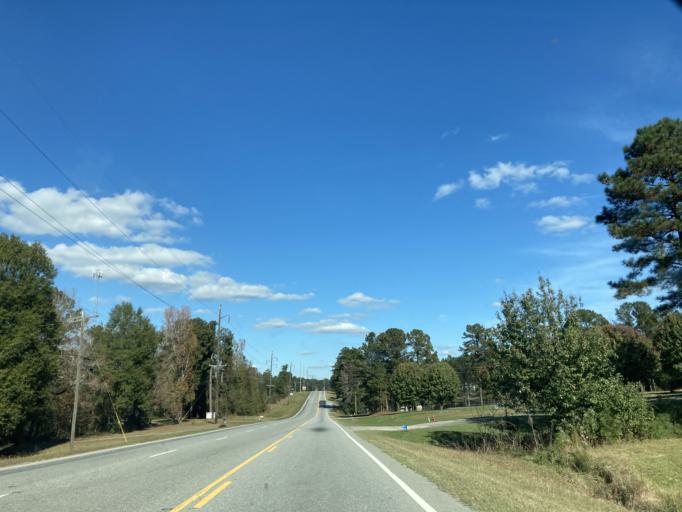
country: US
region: Georgia
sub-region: Jones County
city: Gray
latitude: 32.9132
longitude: -83.5177
